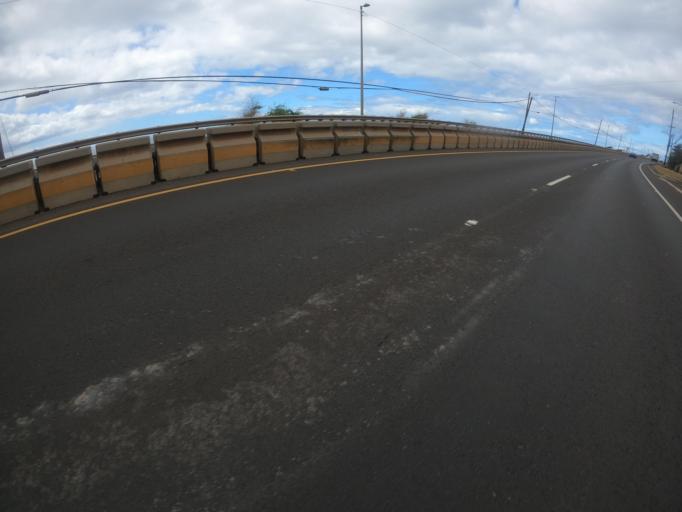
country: US
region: Hawaii
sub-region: Honolulu County
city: Ma'ili
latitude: 21.3991
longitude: -158.1725
